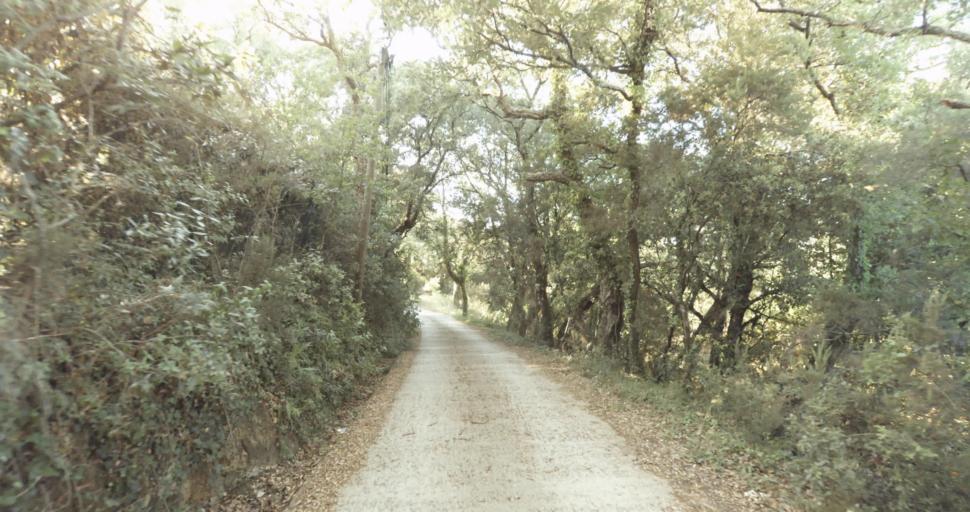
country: FR
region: Provence-Alpes-Cote d'Azur
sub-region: Departement du Var
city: Gassin
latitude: 43.2273
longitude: 6.5953
